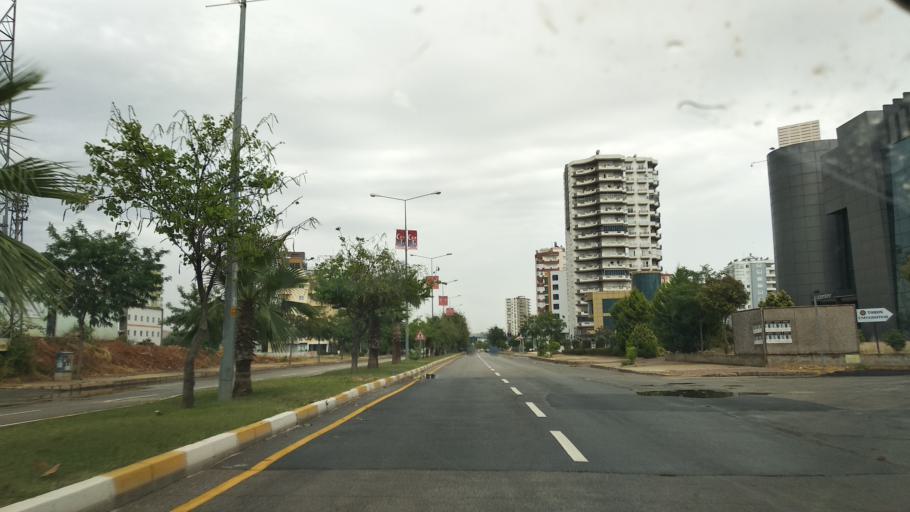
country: TR
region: Mersin
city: Mercin
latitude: 36.7976
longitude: 34.5896
